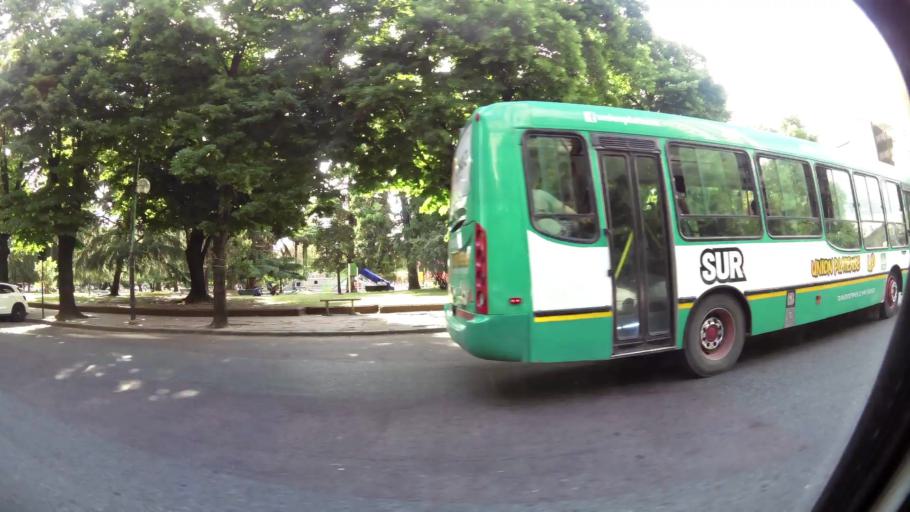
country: AR
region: Buenos Aires
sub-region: Partido de La Plata
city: La Plata
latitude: -34.9161
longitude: -57.9464
